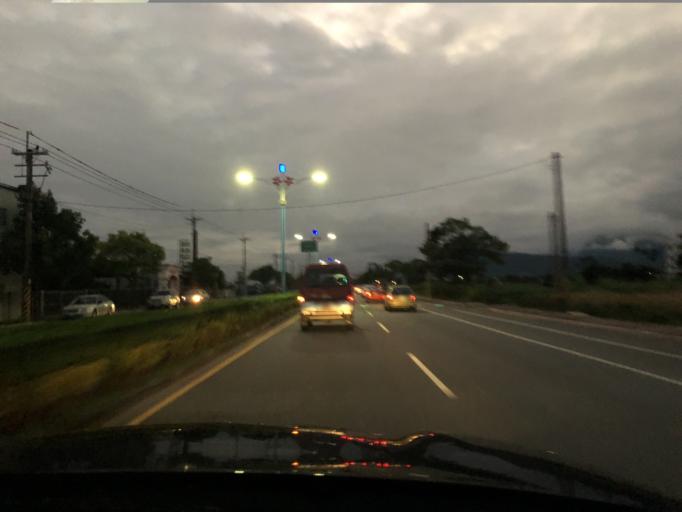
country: TW
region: Taiwan
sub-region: Hualien
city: Hualian
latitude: 23.9688
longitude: 121.5697
